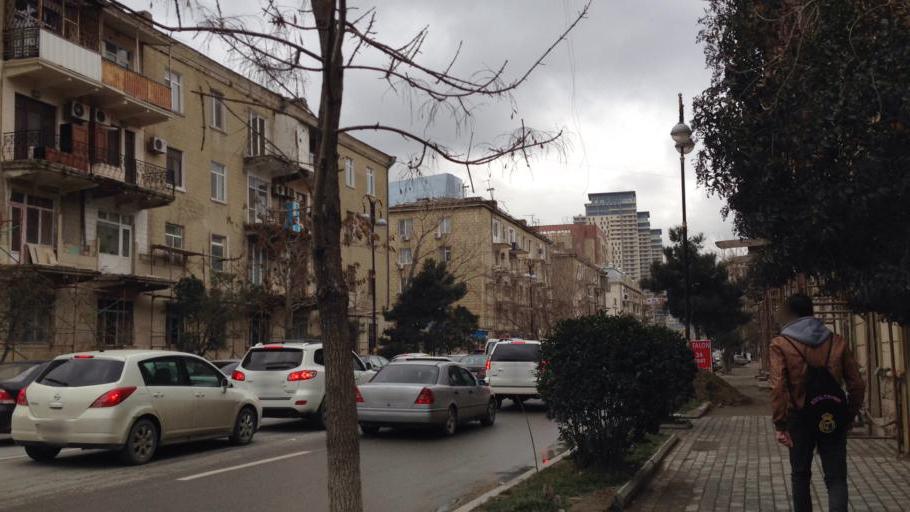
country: AZ
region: Baki
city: Baku
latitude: 40.3782
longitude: 49.8683
